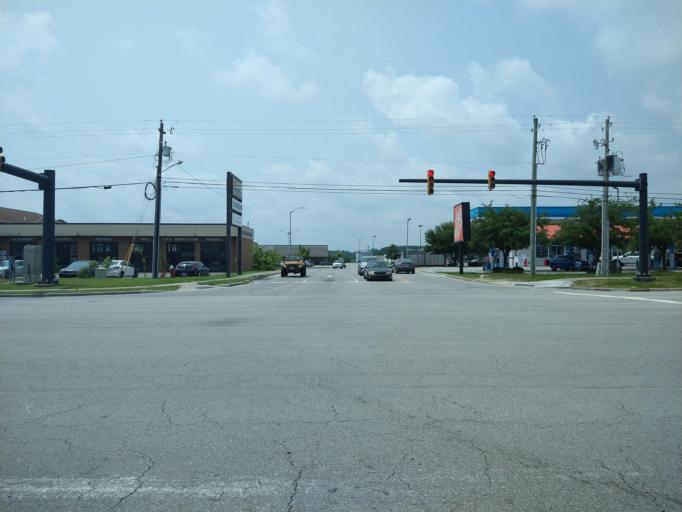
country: US
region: North Carolina
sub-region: Onslow County
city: Pumpkin Center
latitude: 34.7750
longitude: -77.3897
